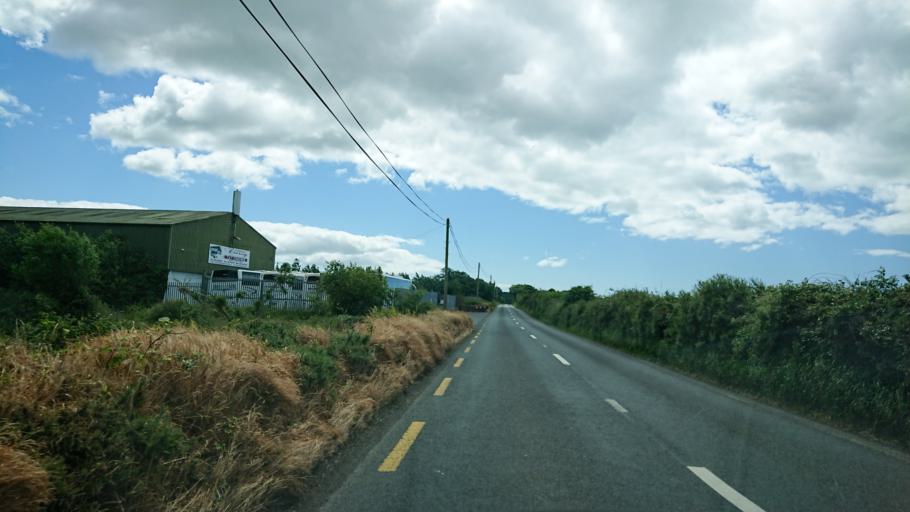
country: IE
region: Munster
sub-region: Waterford
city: Tra Mhor
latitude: 52.1939
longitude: -7.1872
